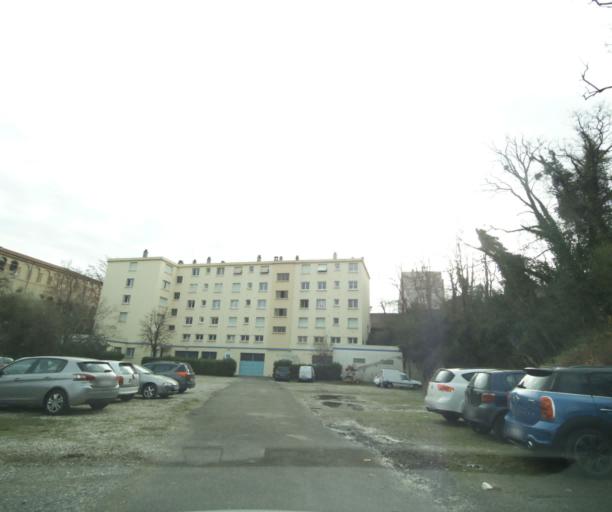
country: FR
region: Rhone-Alpes
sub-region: Departement de la Drome
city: Valence
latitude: 44.9413
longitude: 4.8989
